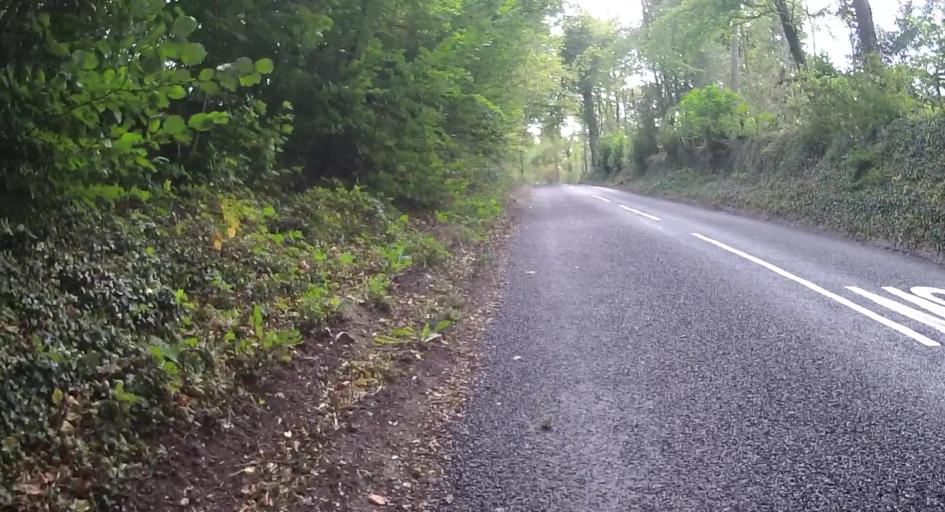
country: GB
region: England
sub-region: Hampshire
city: Kings Worthy
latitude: 51.0772
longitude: -1.1724
